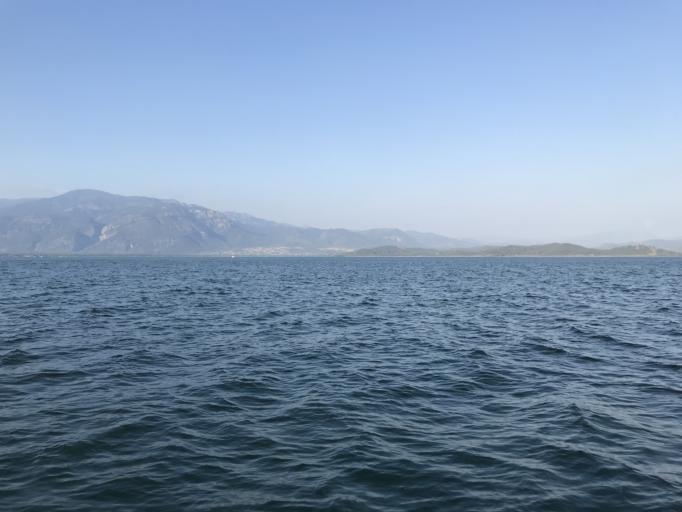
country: TR
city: Dalyan
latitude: 36.9180
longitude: 28.6487
